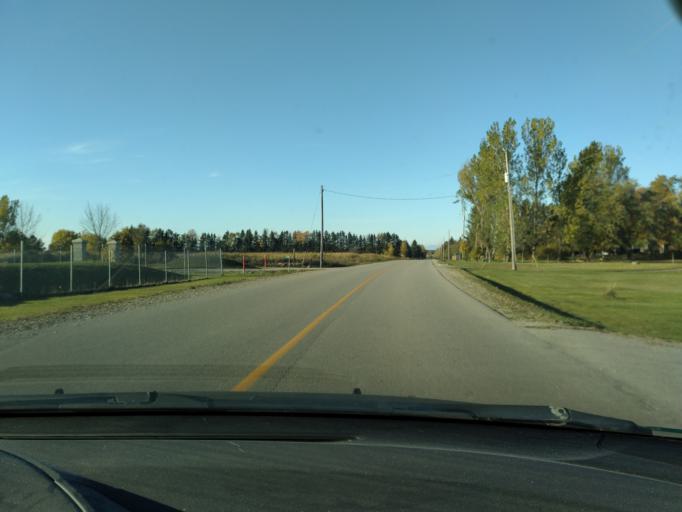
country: CA
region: Ontario
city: Bradford West Gwillimbury
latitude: 44.0209
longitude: -79.7276
